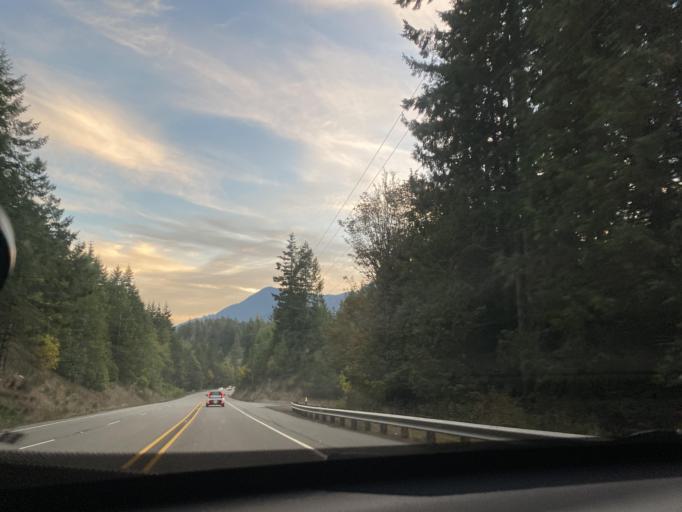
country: US
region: Washington
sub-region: Clallam County
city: Port Angeles
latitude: 48.0761
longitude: -123.5663
